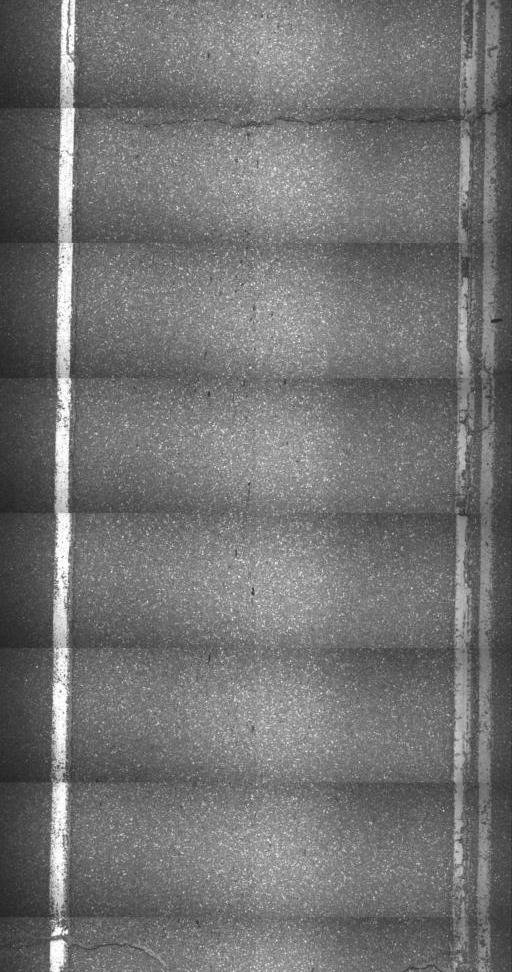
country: US
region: Vermont
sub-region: Orleans County
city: Newport
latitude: 44.9857
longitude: -72.1068
